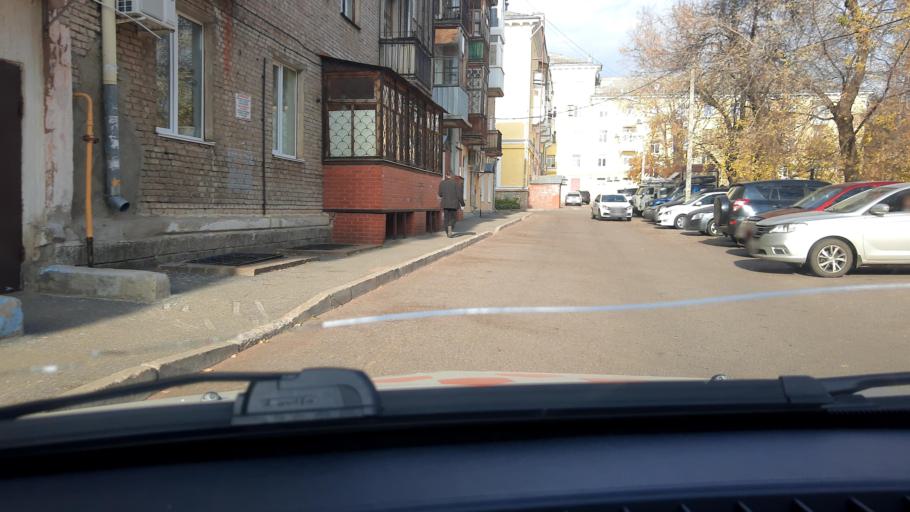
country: RU
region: Bashkortostan
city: Ufa
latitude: 54.8176
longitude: 56.0693
